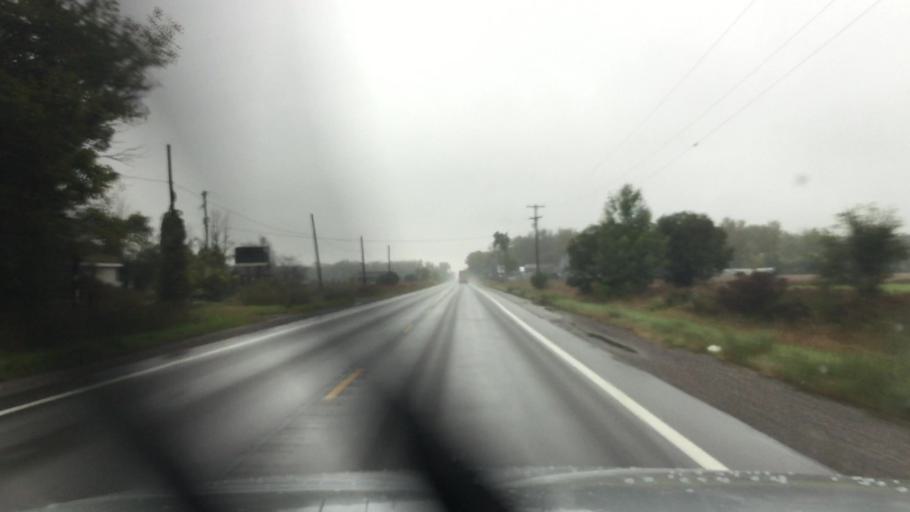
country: US
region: Michigan
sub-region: Saginaw County
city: Saginaw
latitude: 43.3788
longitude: -83.9553
